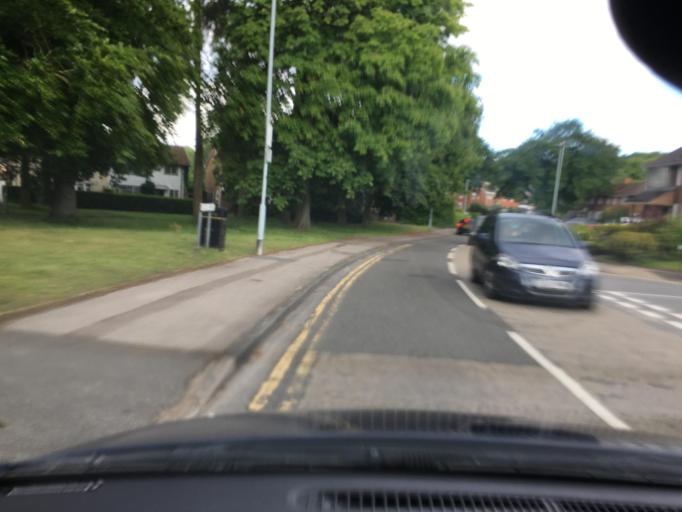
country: GB
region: England
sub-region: Bracknell Forest
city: Bracknell
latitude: 51.4001
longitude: -0.7546
